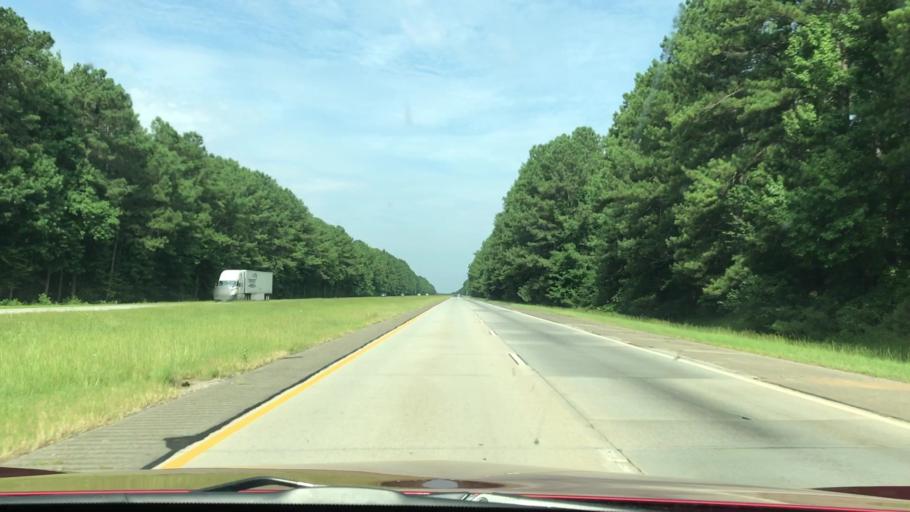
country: US
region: Georgia
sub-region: Warren County
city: Firing Range
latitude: 33.5039
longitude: -82.7331
